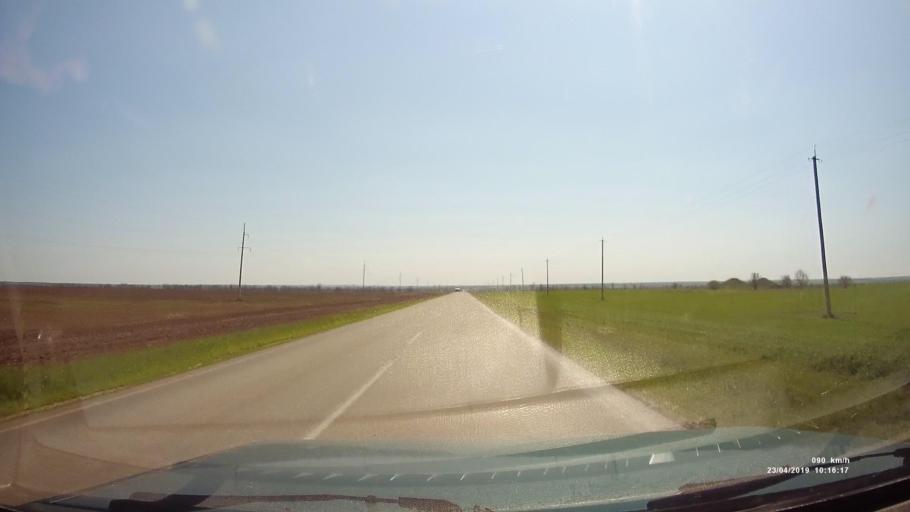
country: RU
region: Rostov
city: Sovetskoye
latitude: 46.6594
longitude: 42.3932
